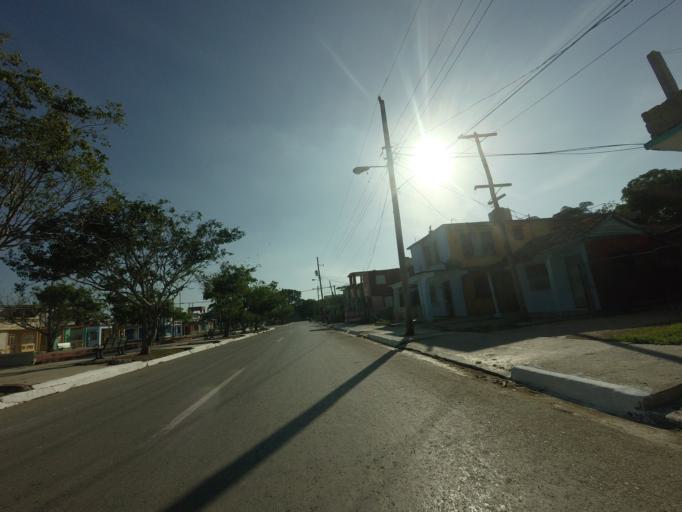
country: CU
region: Ciego de Avila
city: Ciego de Avila
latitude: 21.8450
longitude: -78.7712
